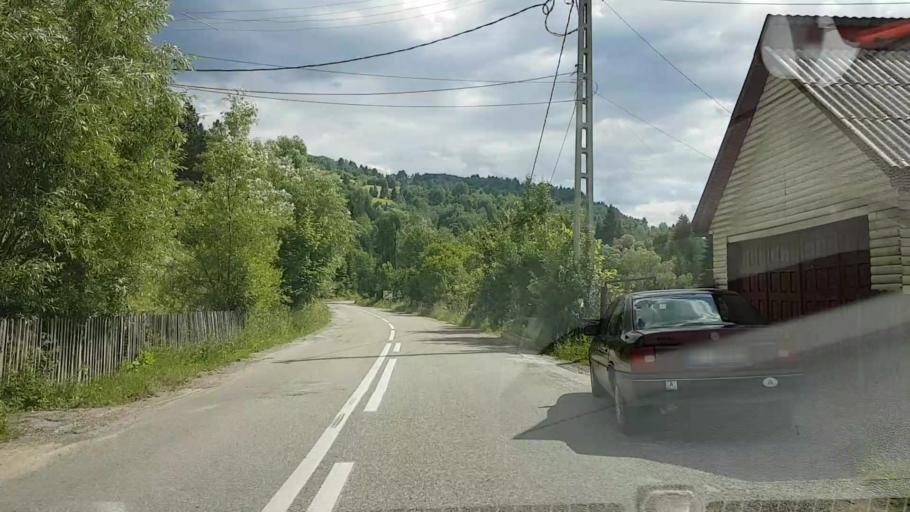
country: RO
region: Neamt
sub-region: Comuna Poiana Teiului
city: Poiana Teiului
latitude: 47.0845
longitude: 25.9698
